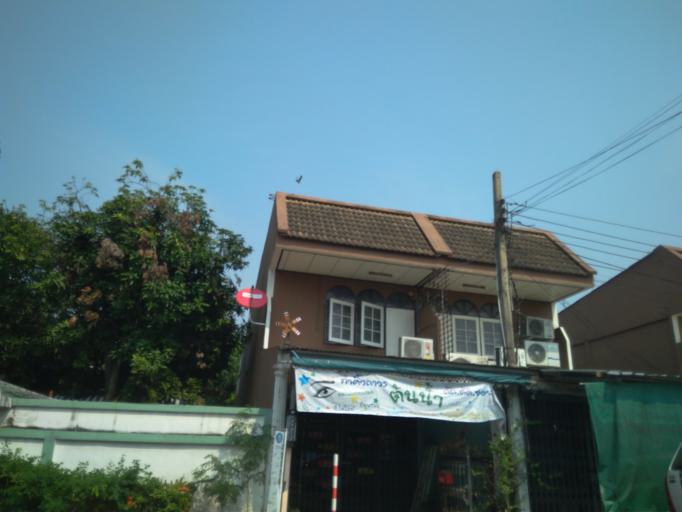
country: TH
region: Bangkok
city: Taling Chan
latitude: 13.7788
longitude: 100.4456
